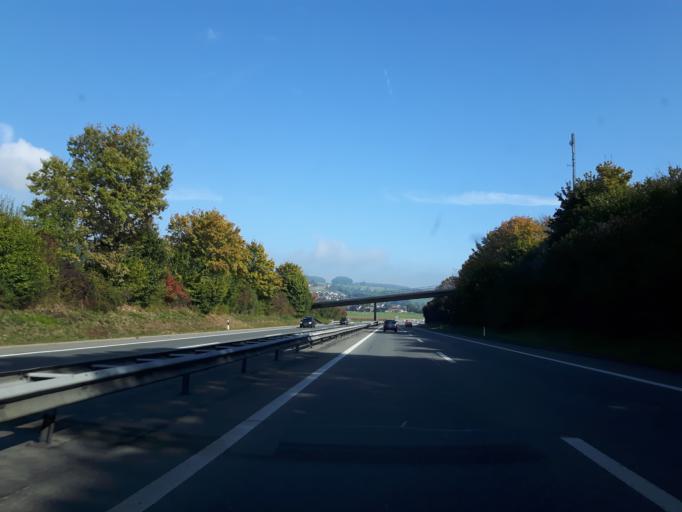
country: CH
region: Lucerne
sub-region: Willisau District
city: Dagmersellen
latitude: 47.2075
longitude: 8.0044
